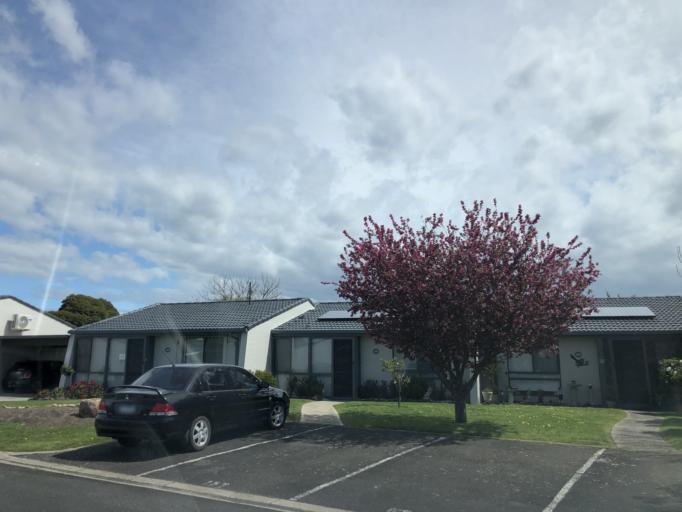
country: AU
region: Victoria
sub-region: Kingston
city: Patterson Lakes
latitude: -38.0729
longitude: 145.1386
